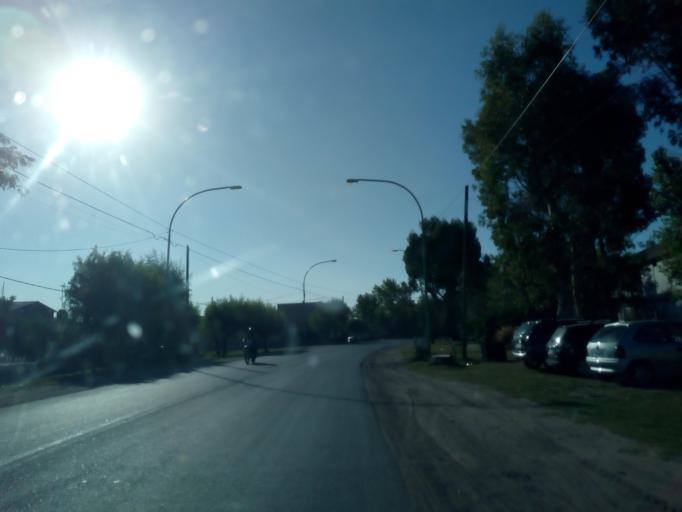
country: AR
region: Buenos Aires
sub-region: Partido de Ensenada
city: Ensenada
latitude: -34.8246
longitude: -57.9622
